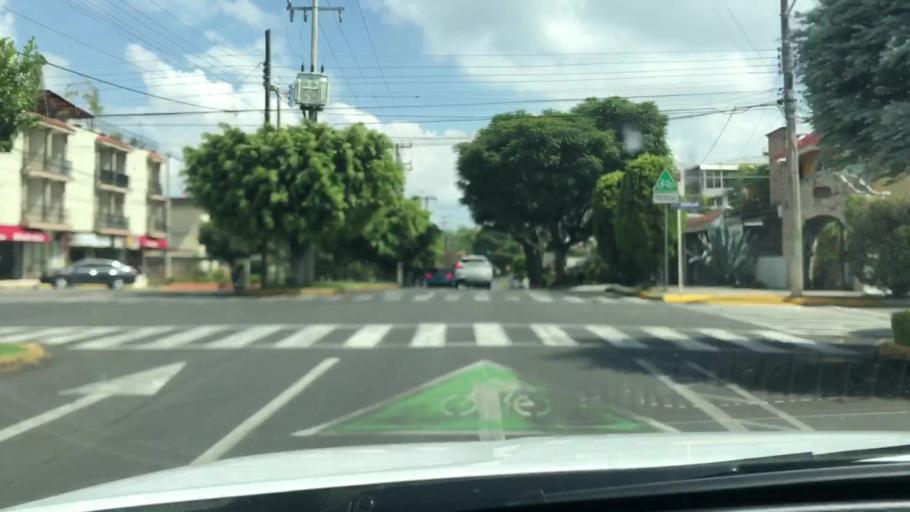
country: MX
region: Jalisco
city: Guadalajara
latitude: 20.6580
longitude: -103.4085
